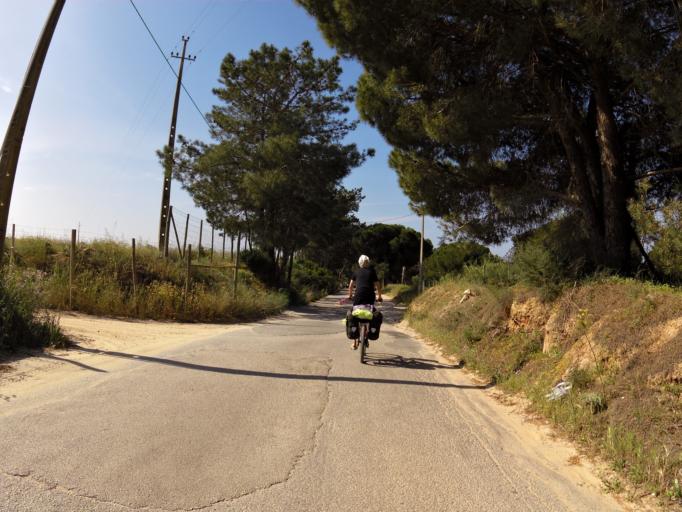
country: PT
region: Faro
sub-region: Loule
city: Almancil
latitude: 37.0651
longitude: -8.0150
